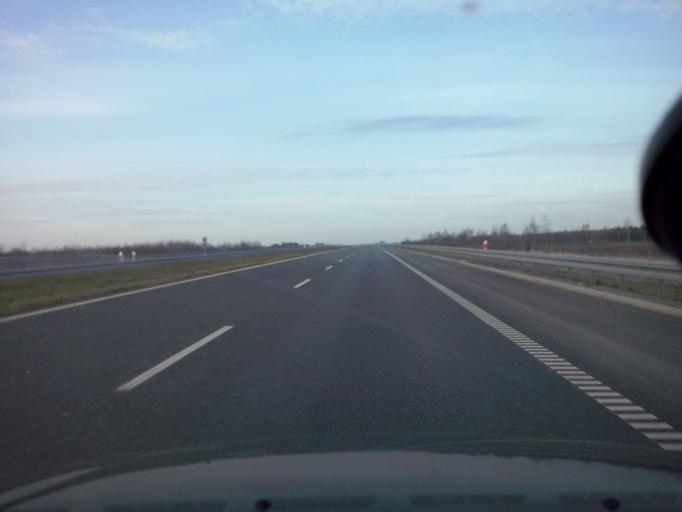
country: PL
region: Subcarpathian Voivodeship
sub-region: Powiat rzeszowski
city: Trzebownisko
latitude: 50.1004
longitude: 22.0151
